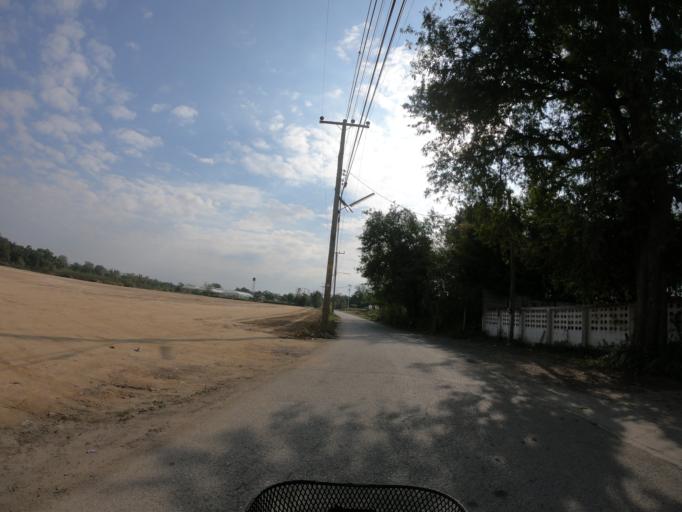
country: TH
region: Chiang Mai
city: San Sai
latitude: 18.8076
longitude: 99.0616
